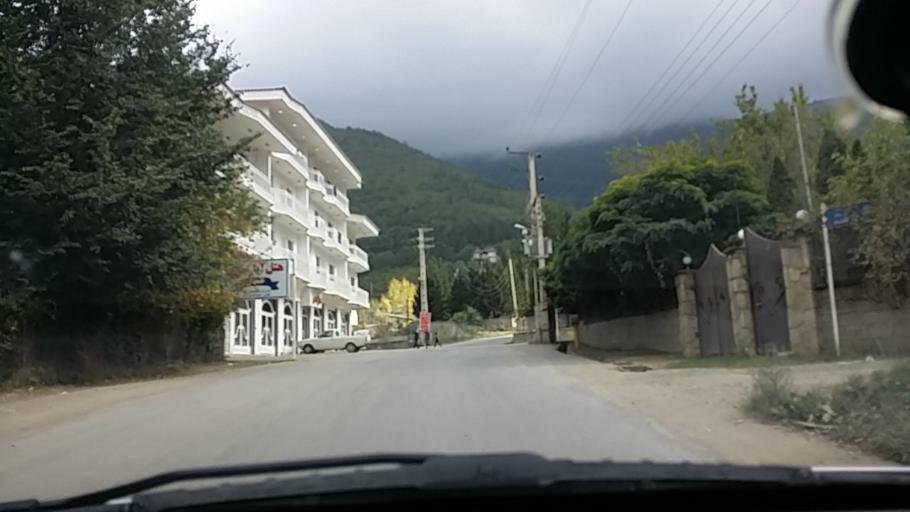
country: IR
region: Mazandaran
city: `Abbasabad
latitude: 36.4973
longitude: 51.1643
